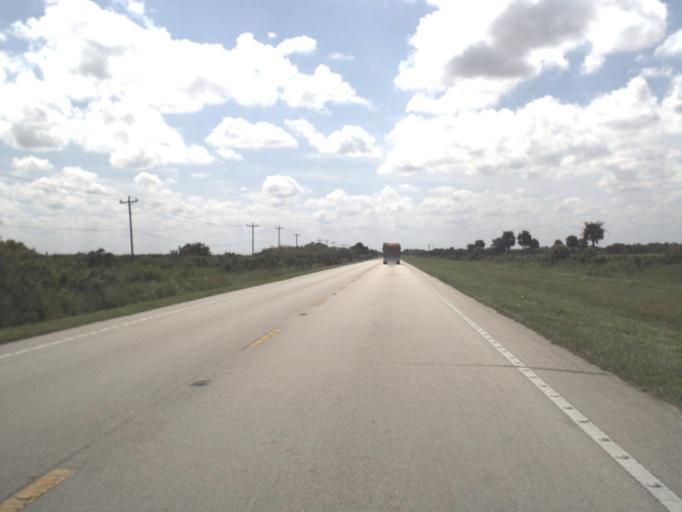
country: US
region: Florida
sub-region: Collier County
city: Immokalee
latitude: 26.5013
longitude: -81.4349
